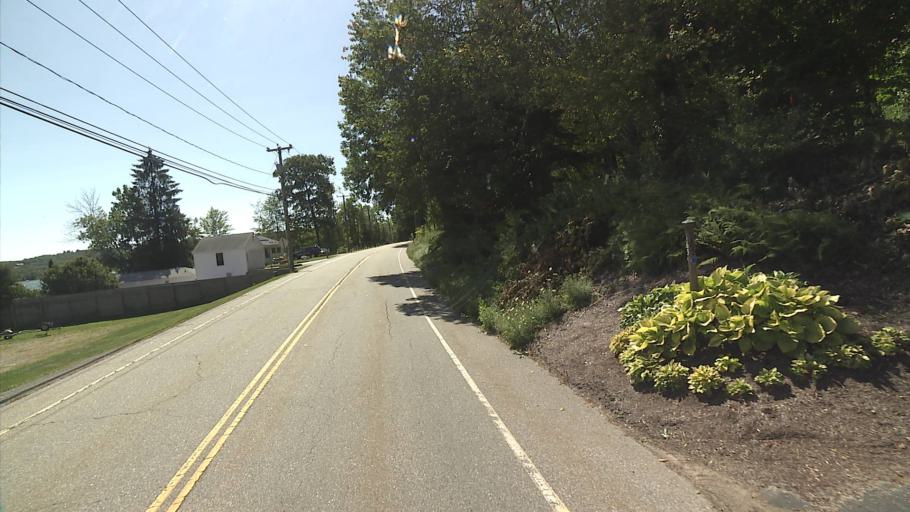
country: US
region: Connecticut
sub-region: Litchfield County
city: Bethlehem Village
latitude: 41.6936
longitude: -73.2321
